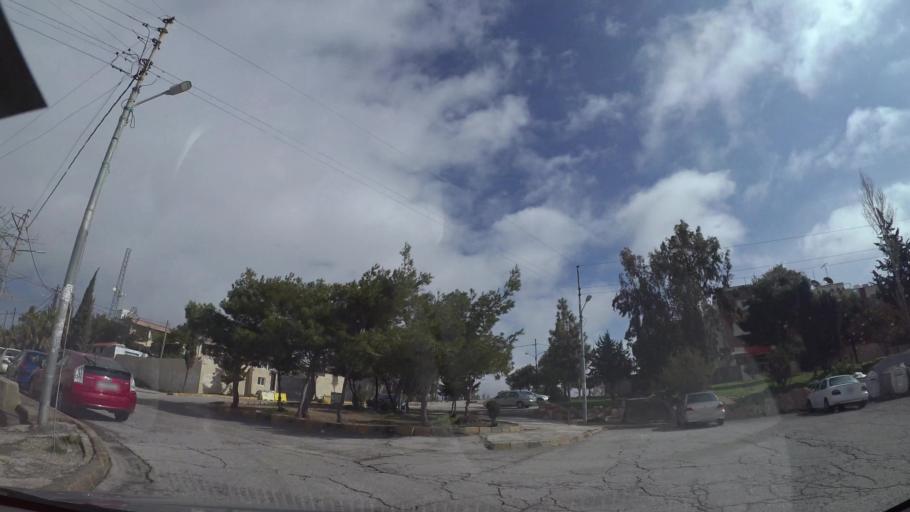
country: JO
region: Amman
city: Al Jubayhah
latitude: 32.0532
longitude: 35.8779
